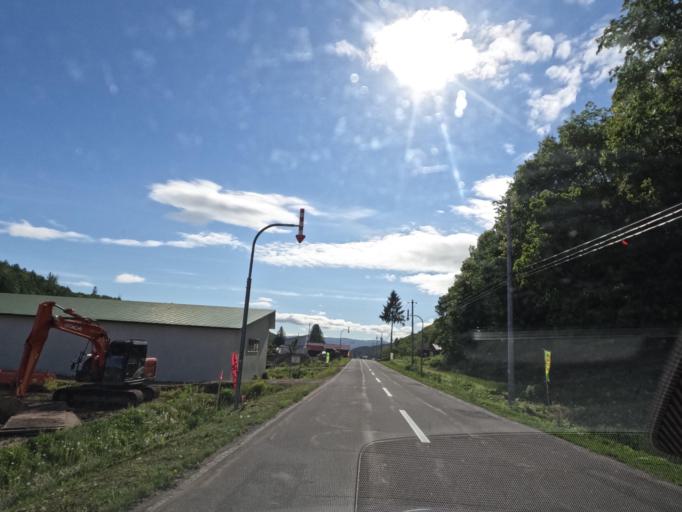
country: JP
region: Hokkaido
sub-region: Asahikawa-shi
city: Asahikawa
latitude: 43.6282
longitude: 142.5301
